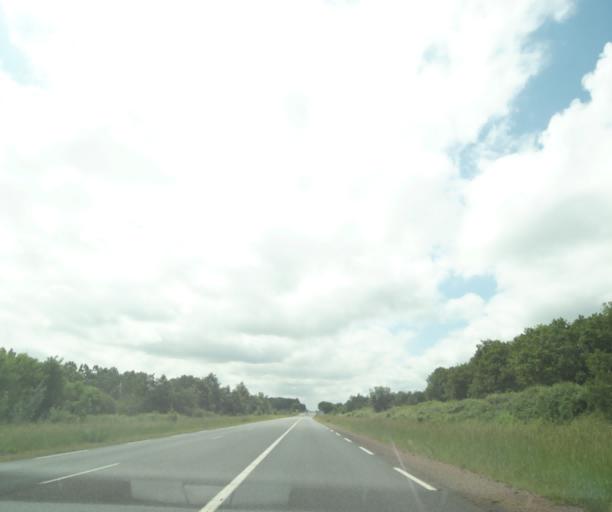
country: FR
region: Poitou-Charentes
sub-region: Departement des Deux-Sevres
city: Airvault
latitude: 46.8017
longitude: -0.2125
